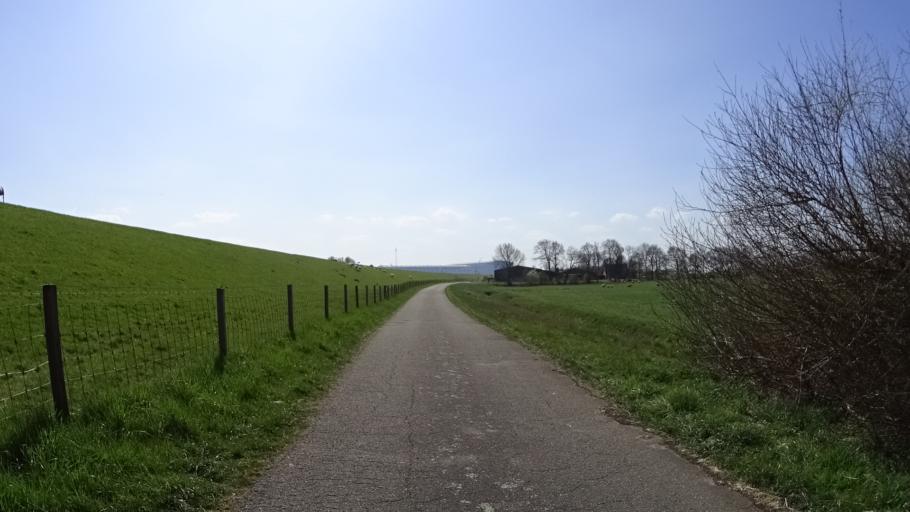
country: DE
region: Lower Saxony
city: Weener
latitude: 53.1164
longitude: 7.3711
